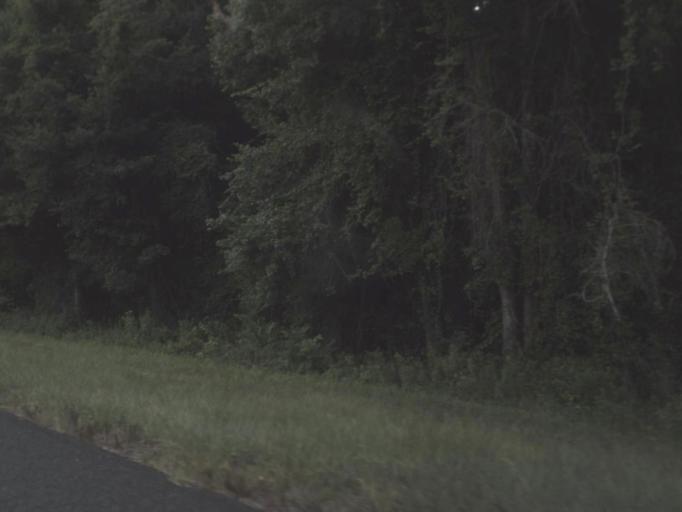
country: US
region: Florida
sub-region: Taylor County
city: Perry
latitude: 30.1674
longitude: -83.6280
